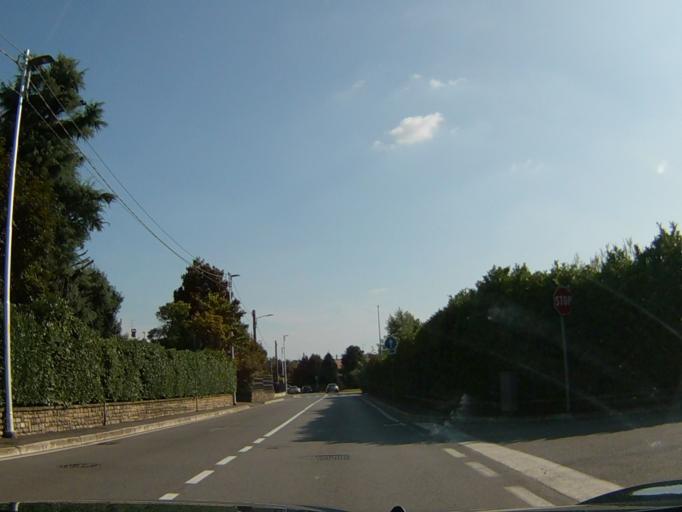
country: IT
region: Lombardy
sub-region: Provincia di Bergamo
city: Telgate
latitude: 45.6284
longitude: 9.8595
